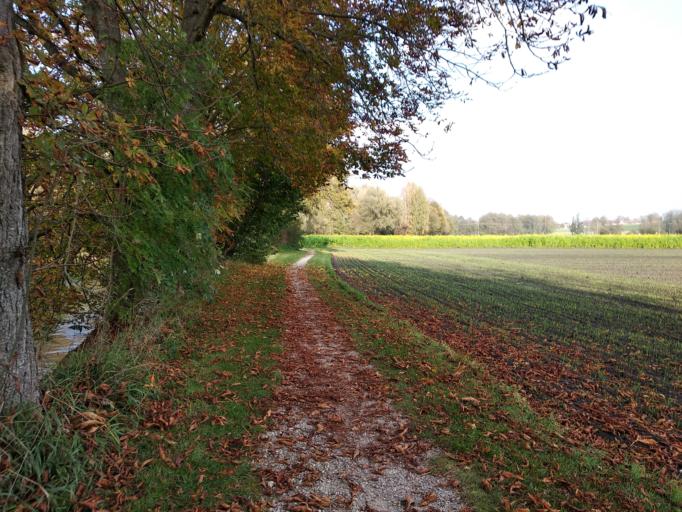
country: DE
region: Bavaria
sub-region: Upper Bavaria
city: Worth
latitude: 48.2366
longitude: 11.8908
